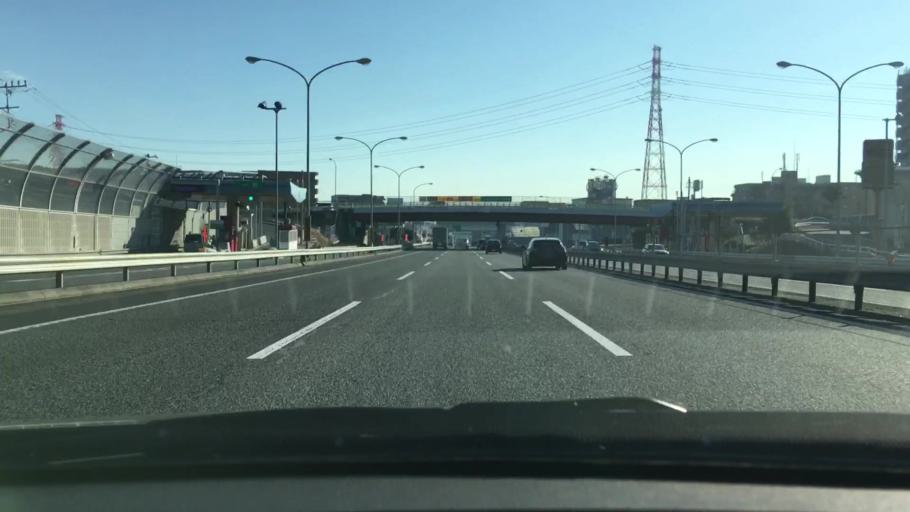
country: JP
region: Chiba
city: Funabashi
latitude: 35.7039
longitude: 139.9507
